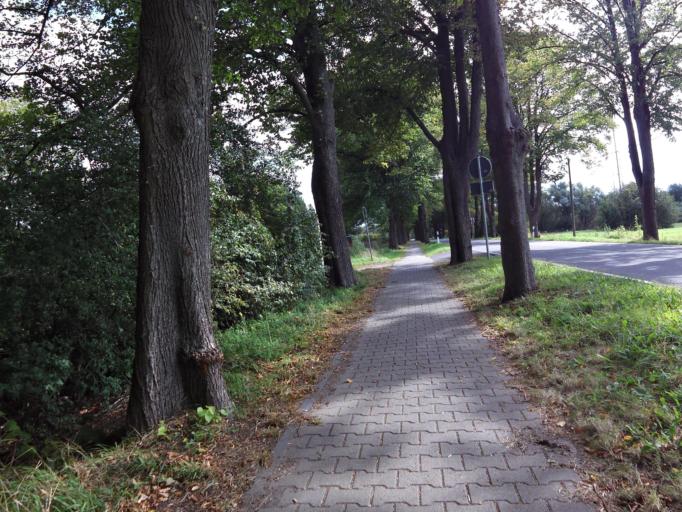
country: DE
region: Saxony-Anhalt
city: Havelberg
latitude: 52.8234
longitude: 12.0646
